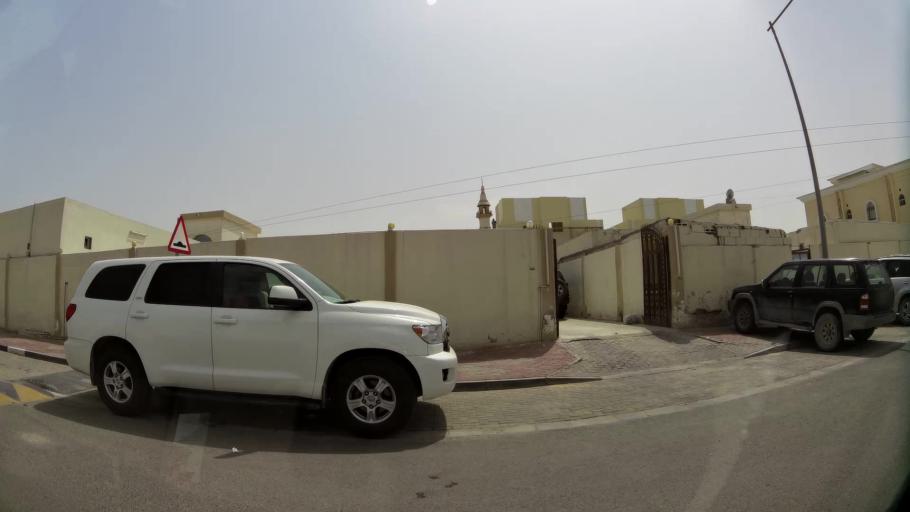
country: QA
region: Baladiyat ar Rayyan
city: Ar Rayyan
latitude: 25.2340
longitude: 51.4295
